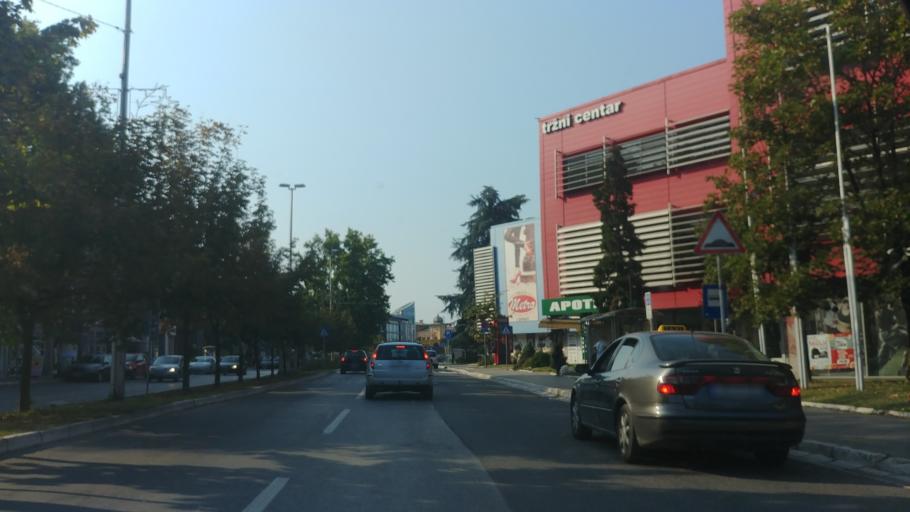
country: BA
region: Brcko
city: Brcko
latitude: 44.8755
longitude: 18.8126
